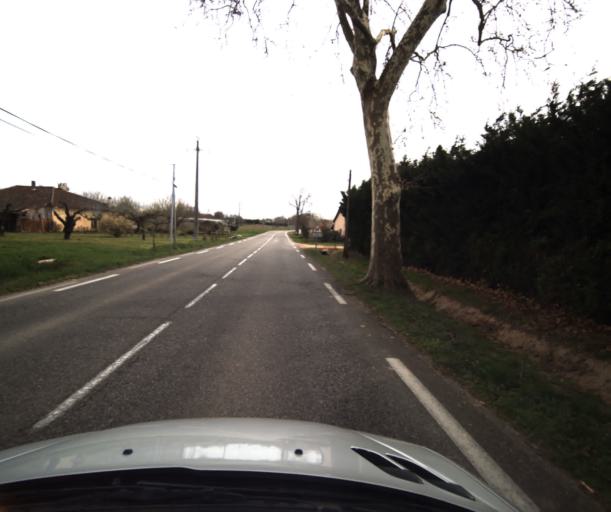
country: FR
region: Midi-Pyrenees
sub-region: Departement du Tarn-et-Garonne
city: Montbeton
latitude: 44.0639
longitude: 1.2876
